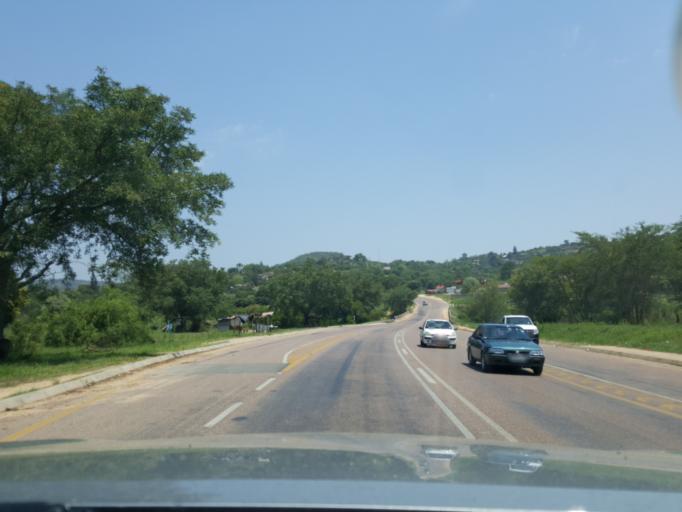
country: ZA
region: Mpumalanga
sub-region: Ehlanzeni District
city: Graksop
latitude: -24.9878
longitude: 31.1103
